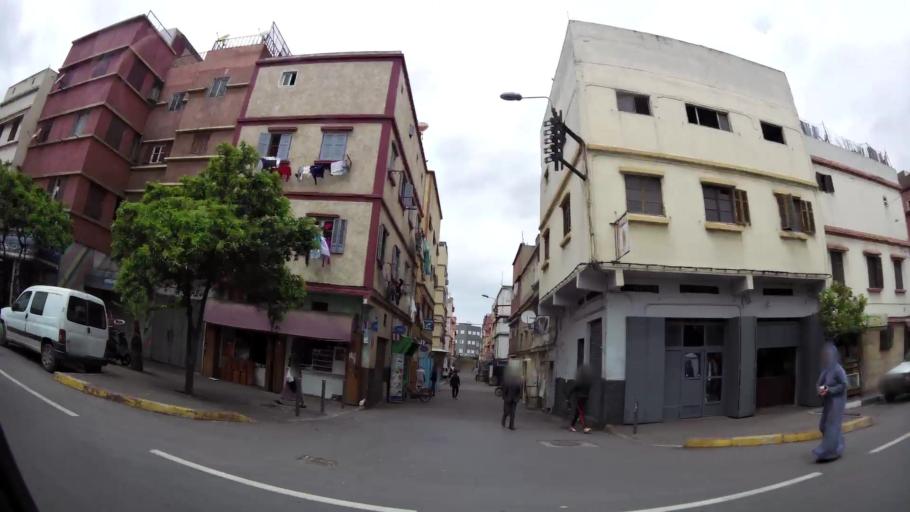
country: MA
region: Grand Casablanca
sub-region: Casablanca
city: Casablanca
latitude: 33.5830
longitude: -7.5562
